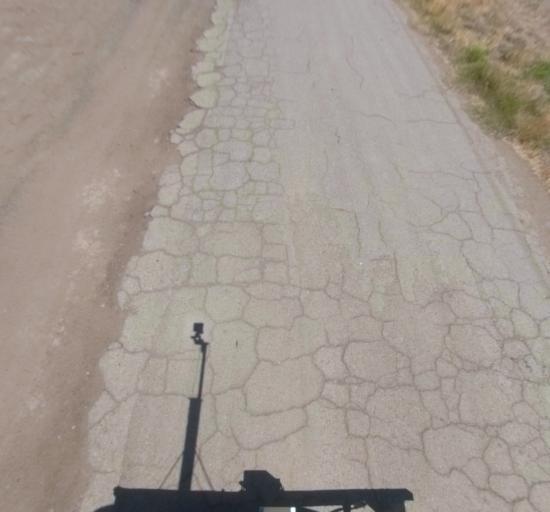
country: US
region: California
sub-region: Madera County
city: Chowchilla
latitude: 37.0047
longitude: -120.3285
